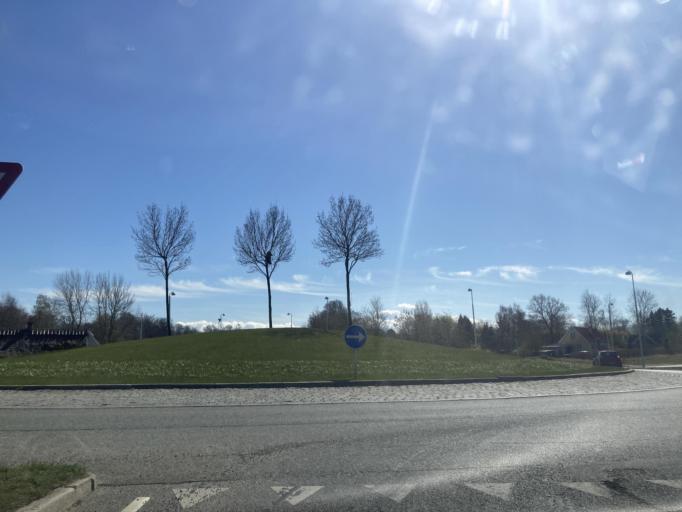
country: DK
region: Capital Region
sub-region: Gribskov Kommune
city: Graested
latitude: 56.0610
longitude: 12.2735
